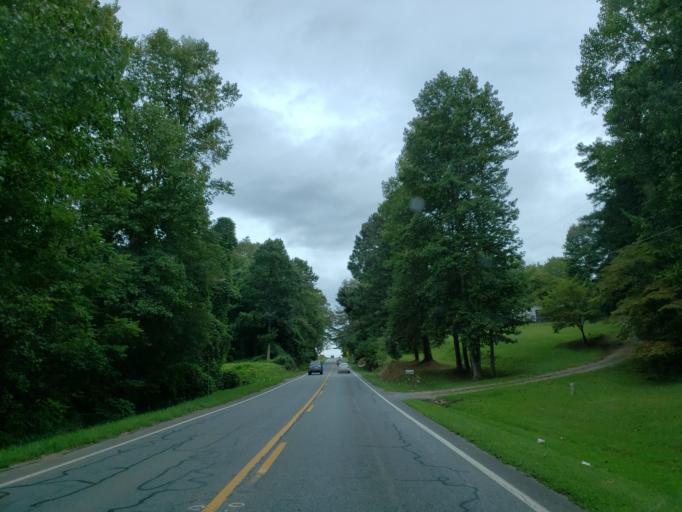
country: US
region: Georgia
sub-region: Gilmer County
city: Ellijay
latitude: 34.6406
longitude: -84.5178
